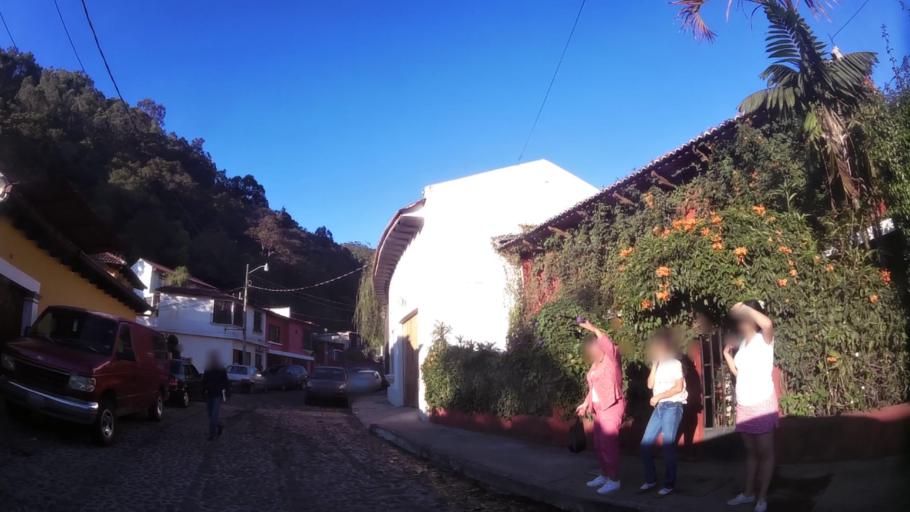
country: GT
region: Sacatepequez
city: Antigua Guatemala
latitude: 14.5631
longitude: -90.7307
